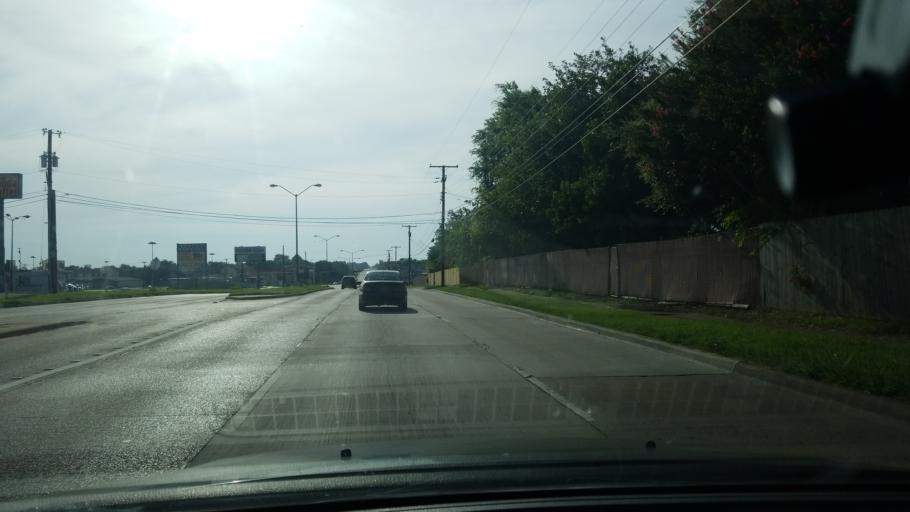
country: US
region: Texas
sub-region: Dallas County
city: Balch Springs
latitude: 32.7486
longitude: -96.6690
